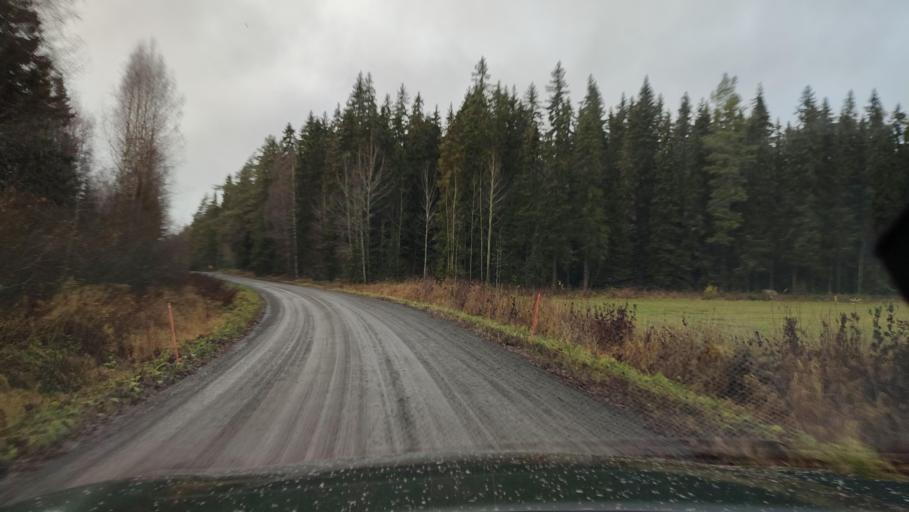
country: FI
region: Ostrobothnia
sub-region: Sydosterbotten
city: Naerpes
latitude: 62.4582
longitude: 21.4984
